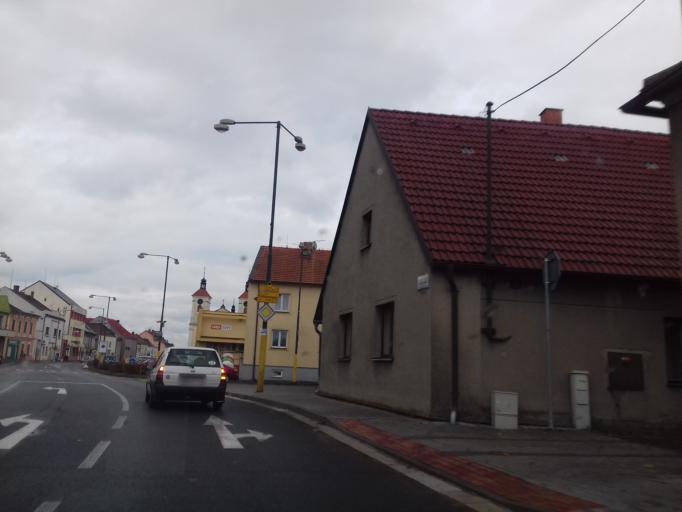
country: CZ
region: Pardubicky
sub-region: Okres Chrudim
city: Chrast
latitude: 49.9018
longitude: 15.9330
